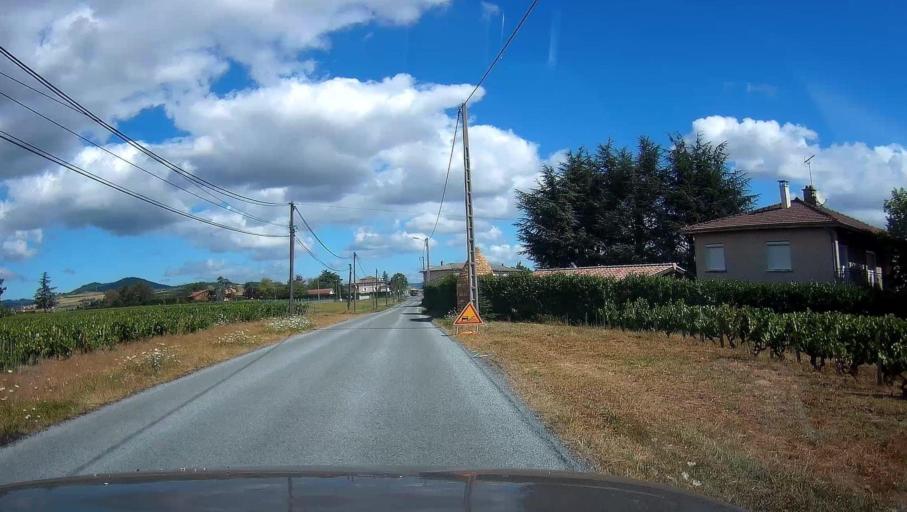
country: FR
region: Rhone-Alpes
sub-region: Departement du Rhone
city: Liergues
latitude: 45.9749
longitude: 4.6510
